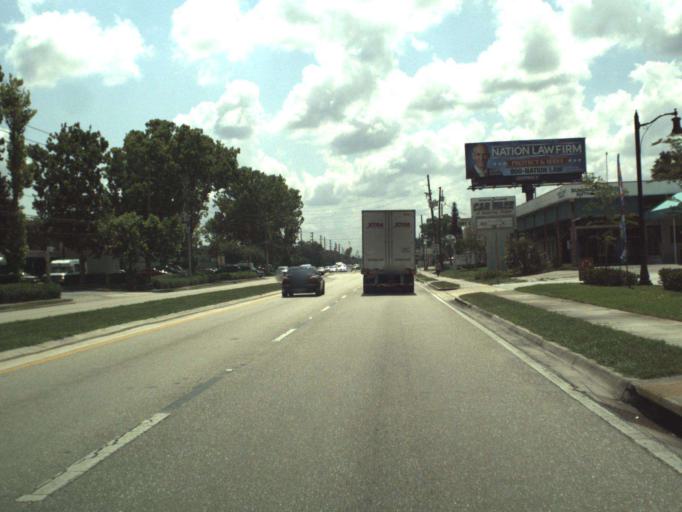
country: US
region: Florida
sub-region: Seminole County
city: Longwood
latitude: 28.6978
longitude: -81.3581
